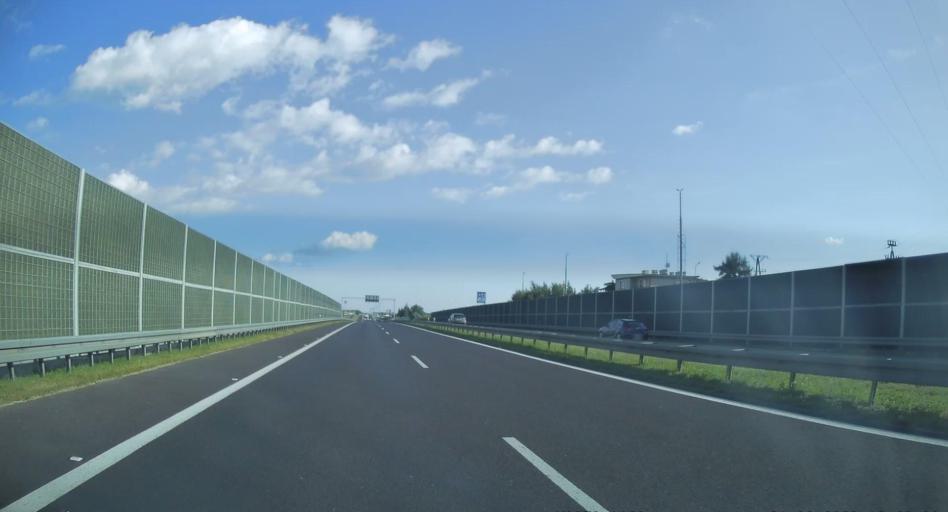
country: PL
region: Masovian Voivodeship
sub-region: Powiat grojecki
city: Goszczyn
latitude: 51.7543
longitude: 20.9068
